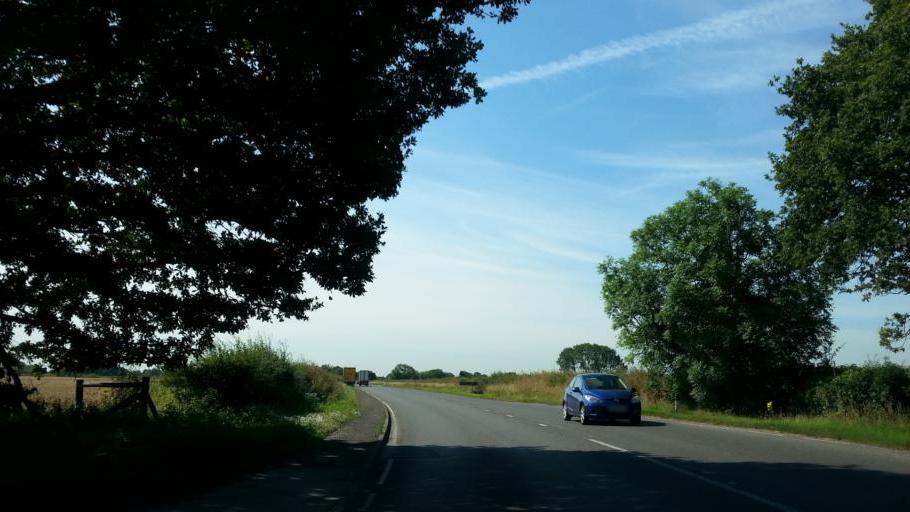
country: GB
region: England
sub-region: Nottinghamshire
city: Newark on Trent
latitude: 53.1154
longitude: -0.8204
